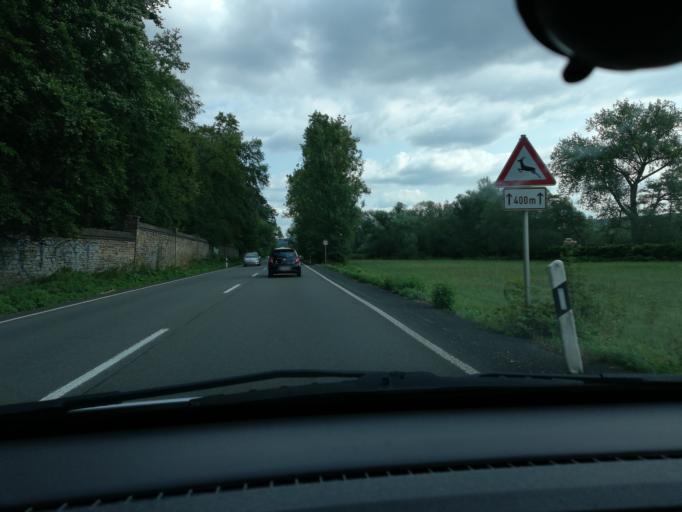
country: DE
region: North Rhine-Westphalia
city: Wetter (Ruhr)
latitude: 51.4002
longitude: 7.3598
